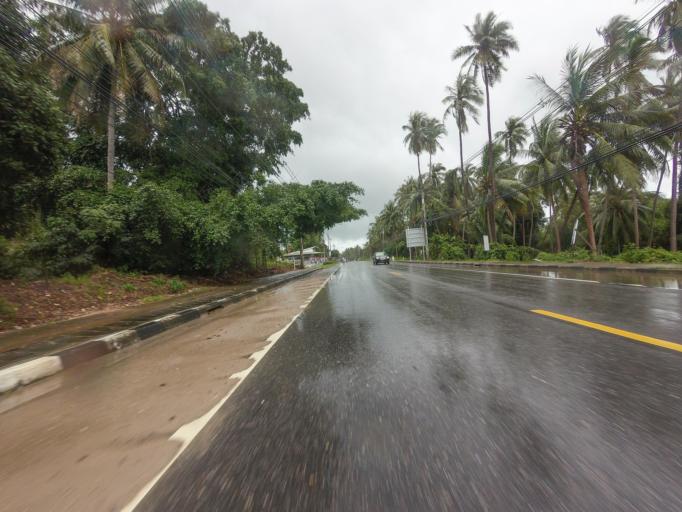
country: TH
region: Surat Thani
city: Ko Samui
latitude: 9.4455
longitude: 100.0089
